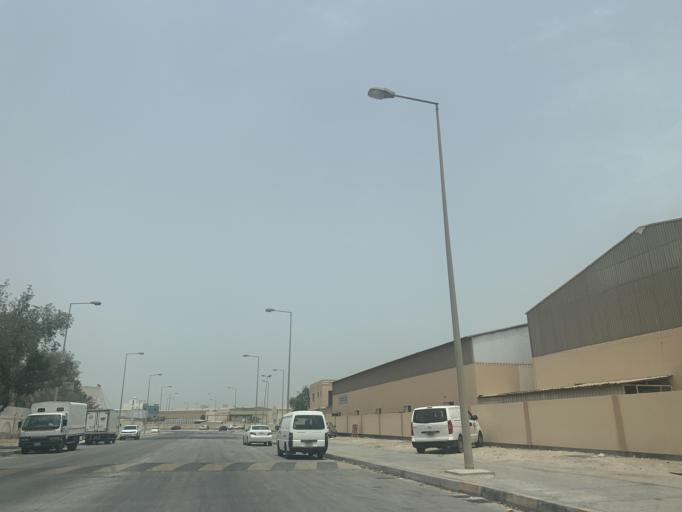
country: BH
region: Northern
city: Sitrah
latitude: 26.1811
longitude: 50.6098
